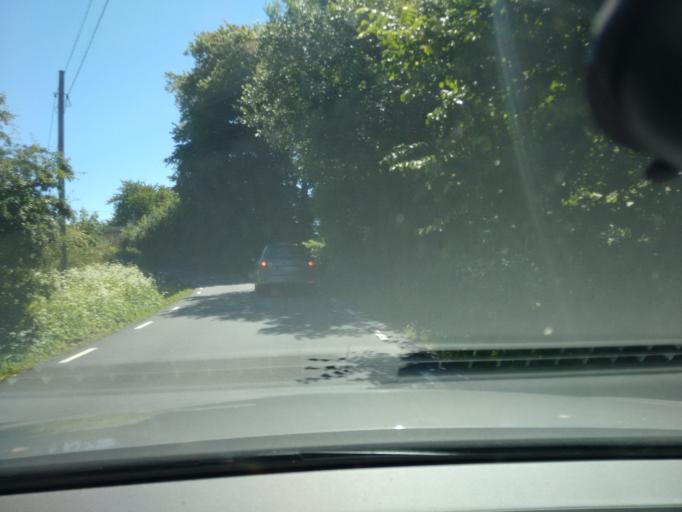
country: SE
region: Skane
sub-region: Kristianstads Kommun
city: Degeberga
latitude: 55.7767
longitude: 14.0979
